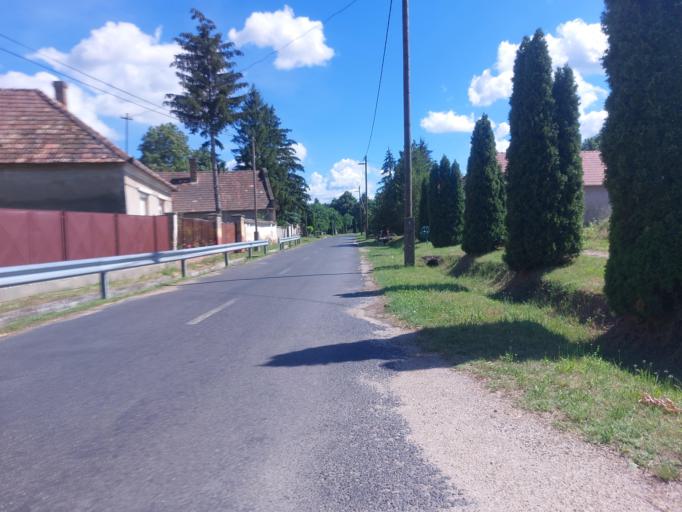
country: HU
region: Veszprem
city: Devecser
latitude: 47.1945
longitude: 17.3516
